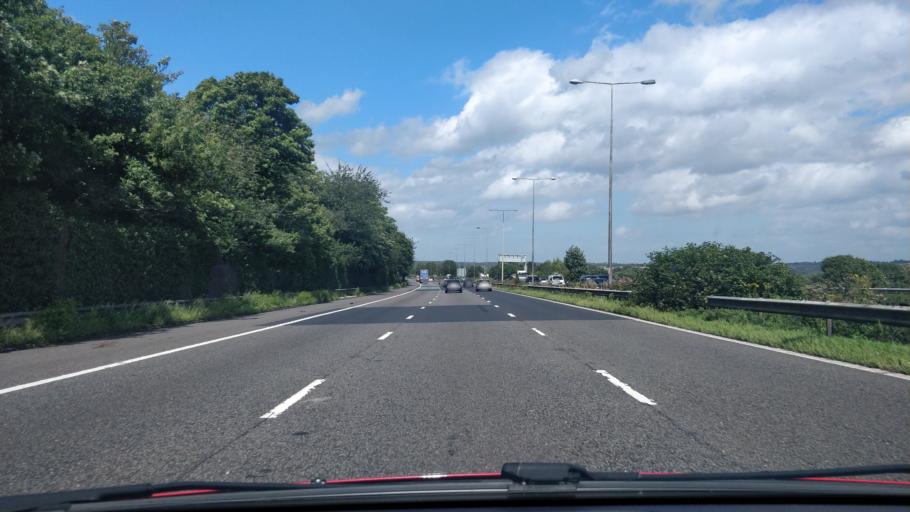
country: GB
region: England
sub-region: Borough of Wigan
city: Shevington
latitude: 53.5428
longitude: -2.6975
